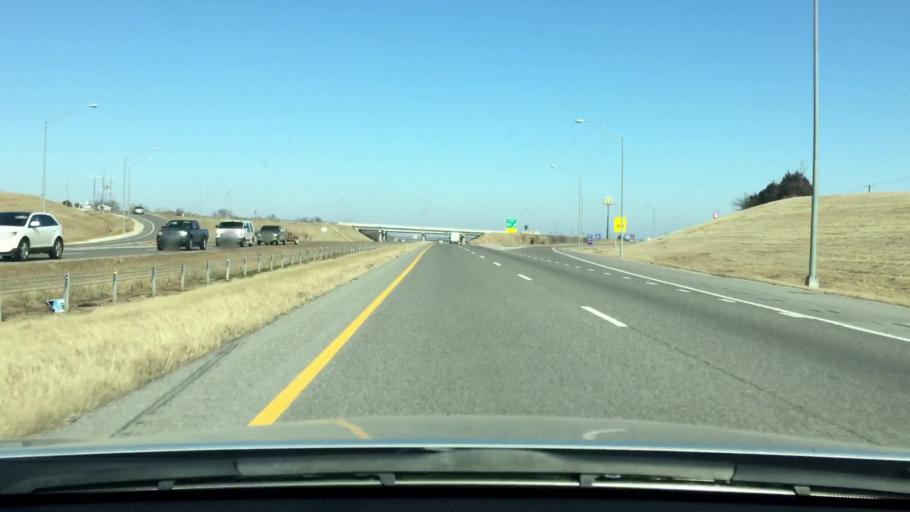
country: US
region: Oklahoma
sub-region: McClain County
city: Purcell
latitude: 34.9790
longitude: -97.3720
